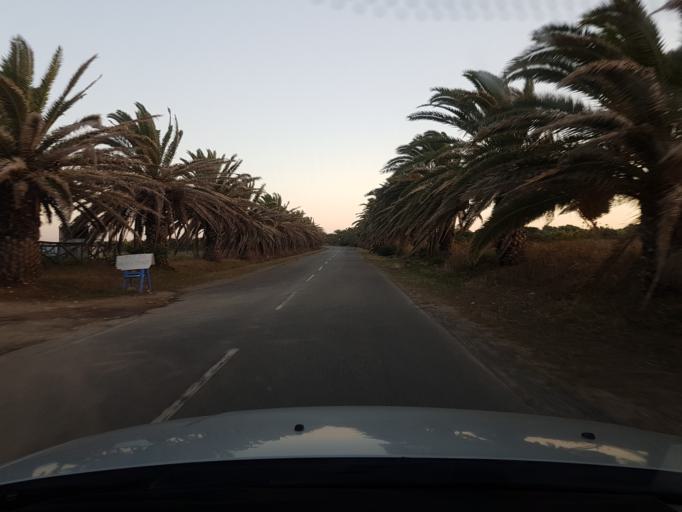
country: IT
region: Sardinia
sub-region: Provincia di Oristano
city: Riola Sardo
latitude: 40.0393
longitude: 8.4010
